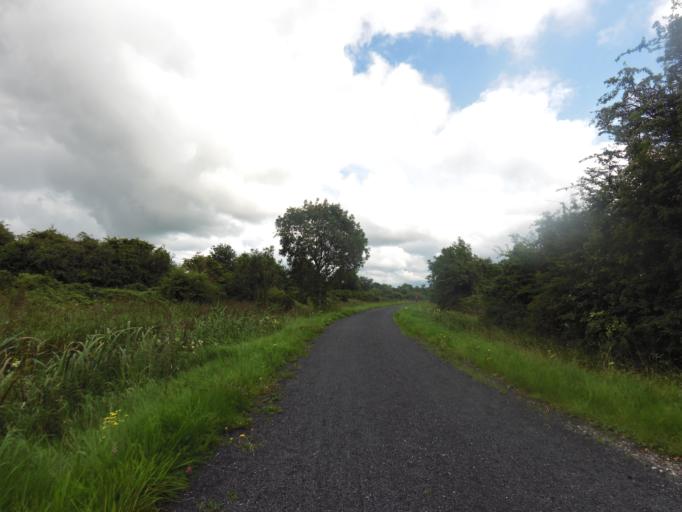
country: IE
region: Leinster
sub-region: An Iarmhi
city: An Muileann gCearr
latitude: 53.5139
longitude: -7.4262
